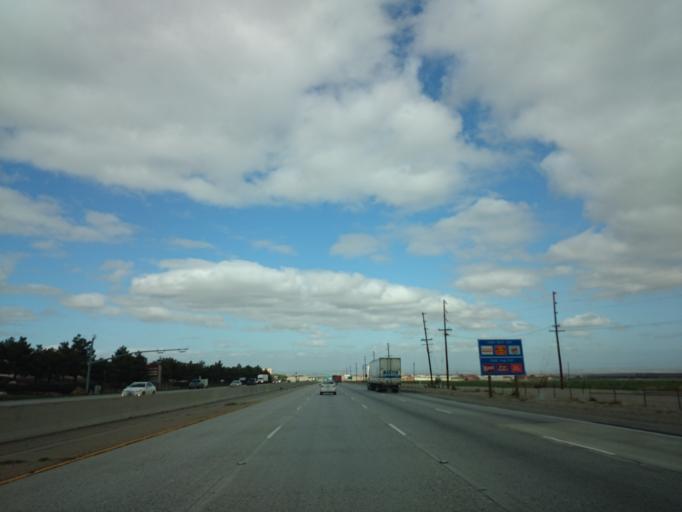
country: US
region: California
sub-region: Kern County
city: Frazier Park
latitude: 34.9749
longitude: -118.9416
